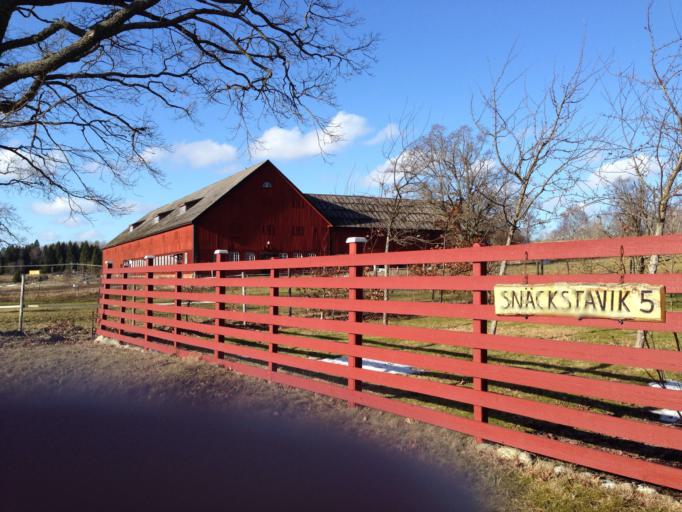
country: SE
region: Stockholm
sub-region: Botkyrka Kommun
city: Varsta
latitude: 59.1201
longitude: 17.7516
